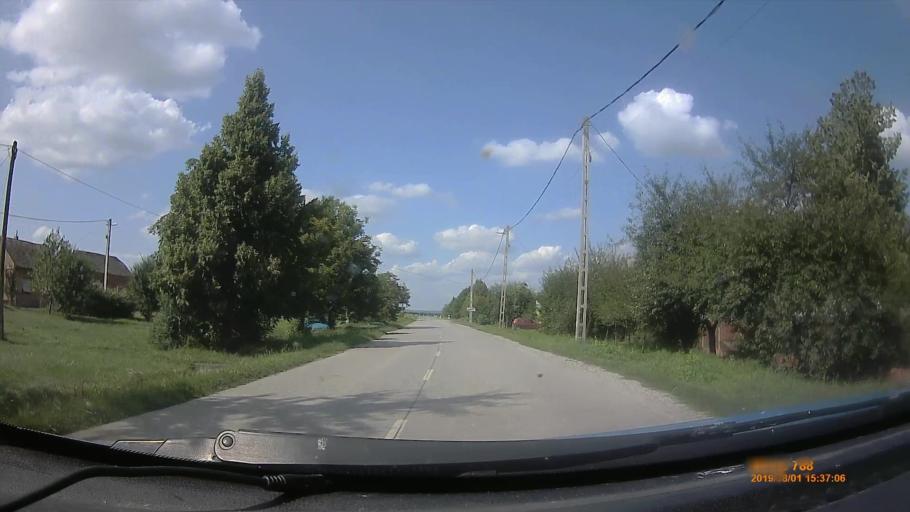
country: HU
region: Baranya
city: Szentlorinc
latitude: 45.9715
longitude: 17.9189
